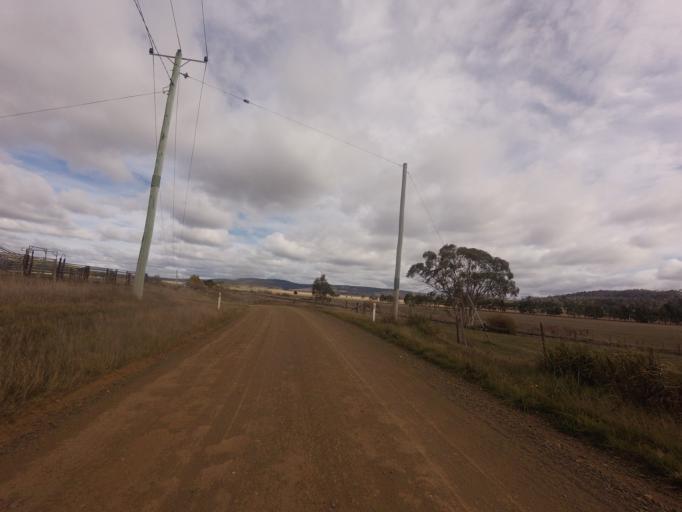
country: AU
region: Tasmania
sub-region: Brighton
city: Bridgewater
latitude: -42.3992
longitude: 147.3913
